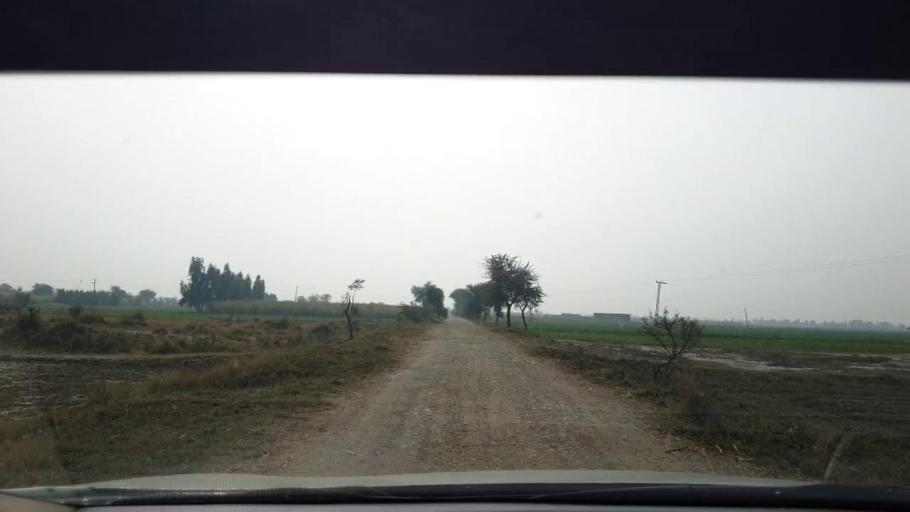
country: PK
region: Sindh
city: Berani
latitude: 25.8442
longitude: 68.8270
